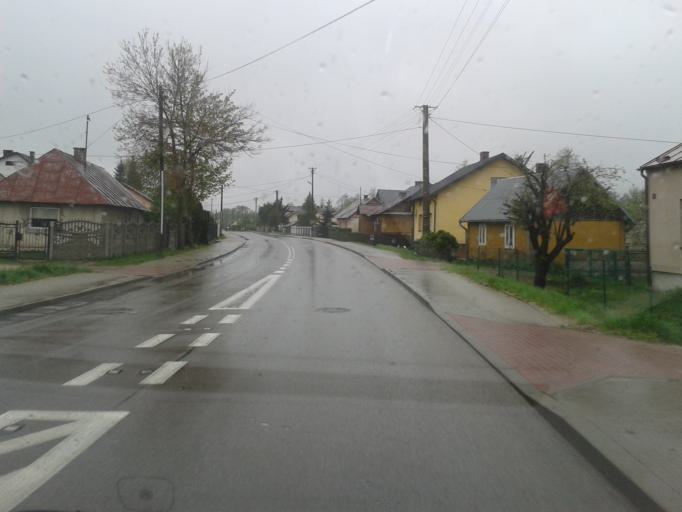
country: PL
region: Lublin Voivodeship
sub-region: Powiat tomaszowski
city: Belzec
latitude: 50.3832
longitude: 23.4177
